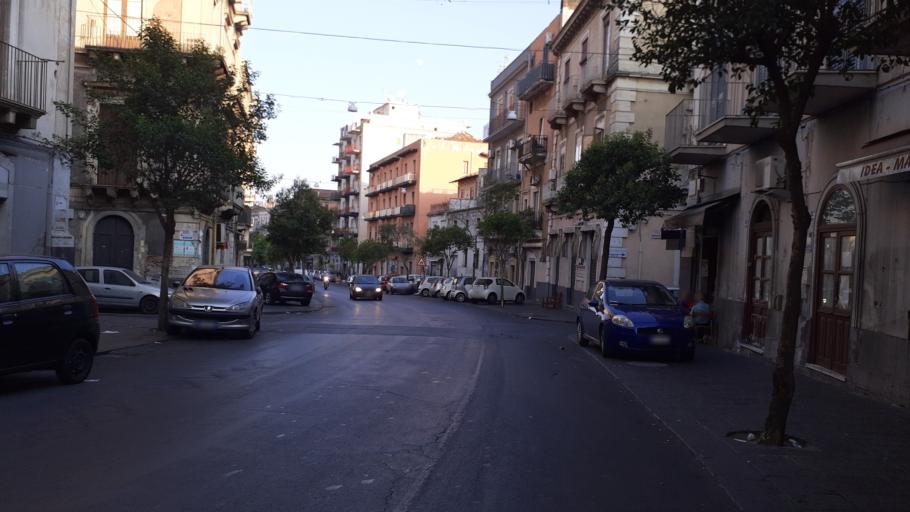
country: IT
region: Sicily
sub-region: Catania
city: Catania
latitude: 37.4998
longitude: 15.0765
